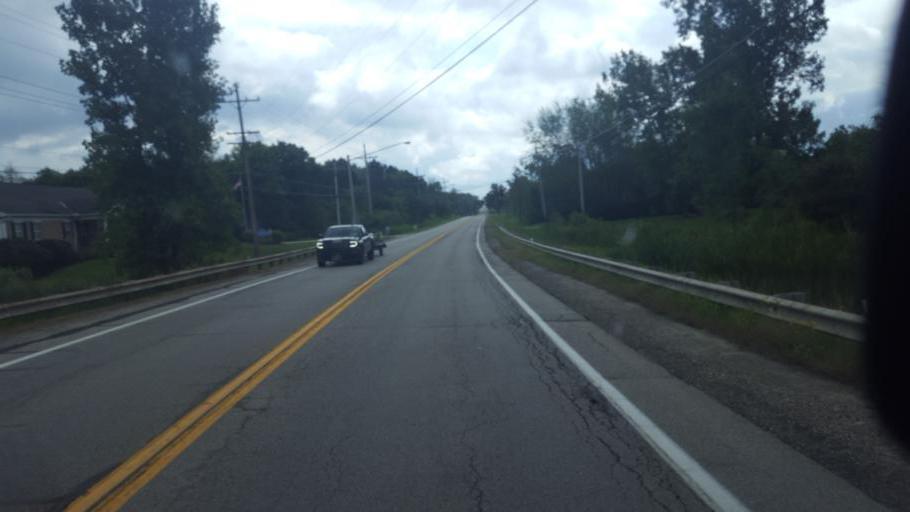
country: US
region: Ohio
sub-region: Geauga County
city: Chardon
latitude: 41.5584
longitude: -81.1976
